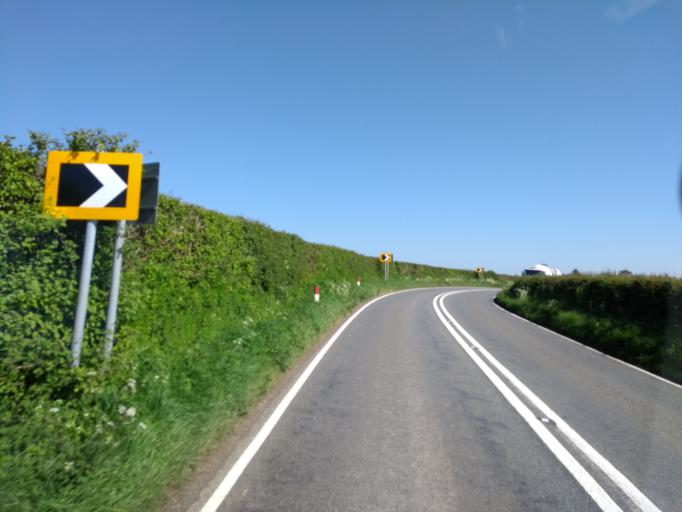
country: GB
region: England
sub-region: Somerset
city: Chard
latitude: 50.8338
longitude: -2.9627
